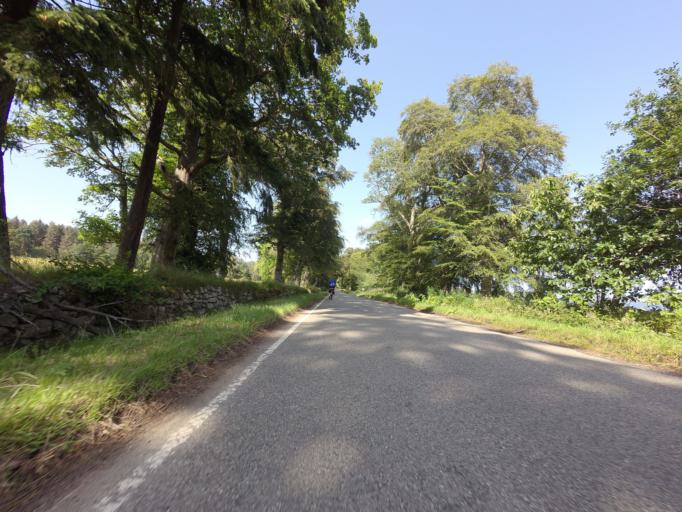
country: GB
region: Scotland
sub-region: Highland
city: Evanton
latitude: 57.6438
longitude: -4.3558
